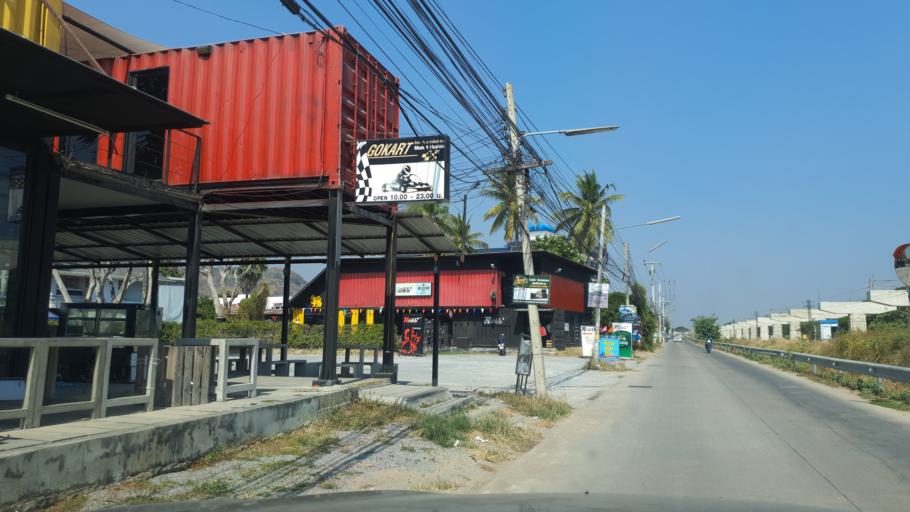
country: TH
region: Prachuap Khiri Khan
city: Hua Hin
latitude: 12.5558
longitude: 99.9573
